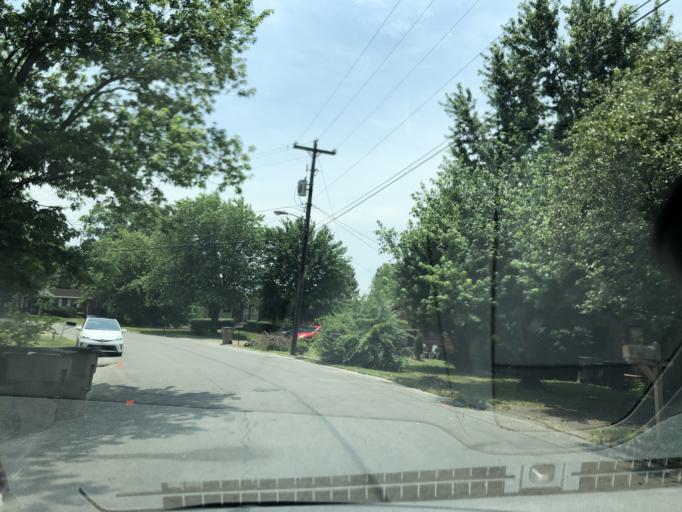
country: US
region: Tennessee
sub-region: Davidson County
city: Oak Hill
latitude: 36.0749
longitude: -86.6745
